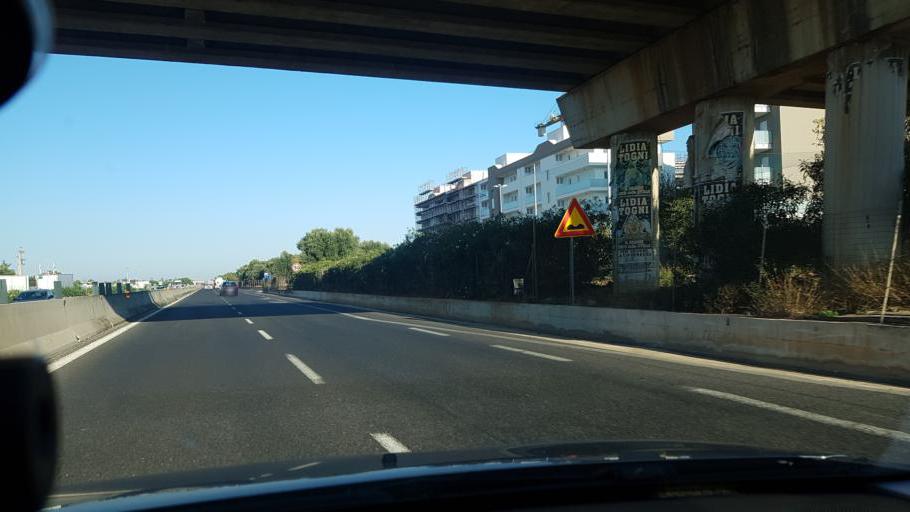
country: IT
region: Apulia
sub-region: Provincia di Bari
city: Monopoli
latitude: 40.9309
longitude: 17.3014
